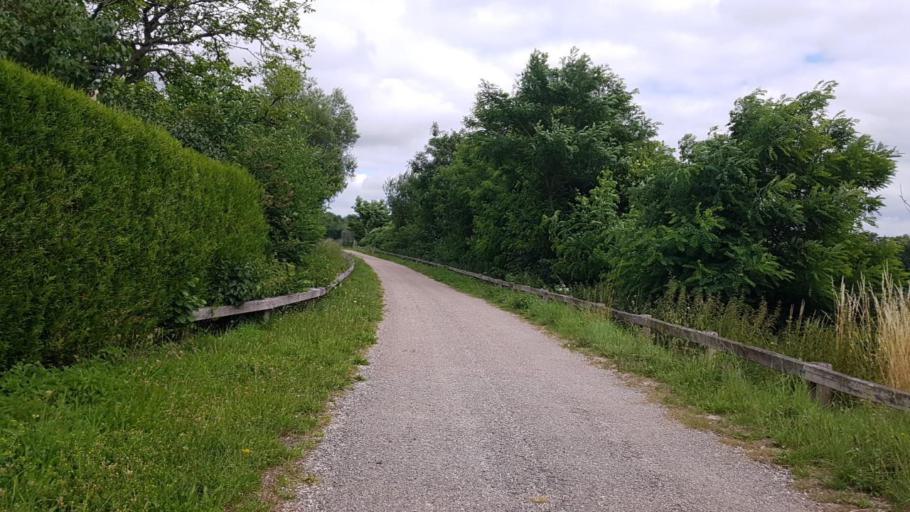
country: FR
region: Picardie
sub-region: Departement de l'Aisne
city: Origny-en-Thierache
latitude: 49.9319
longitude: 4.0110
